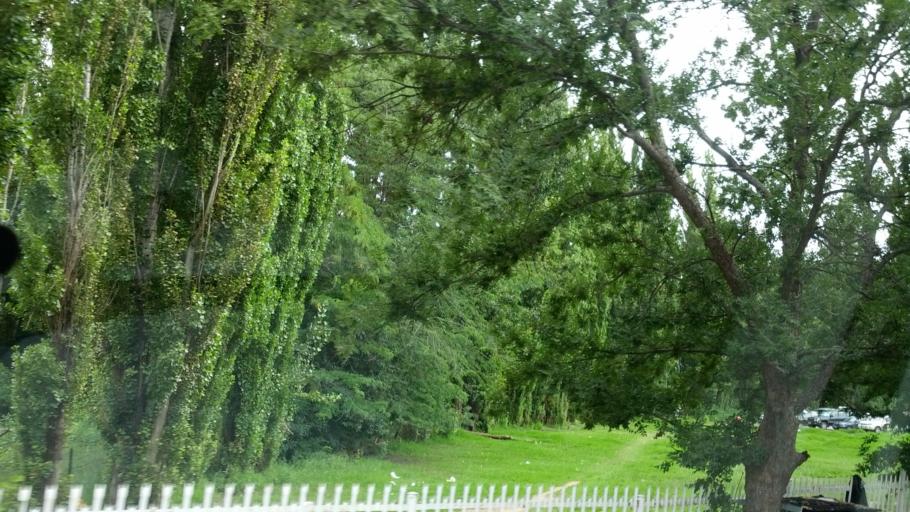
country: LS
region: Maseru
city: Maseru
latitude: -29.3164
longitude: 27.4814
